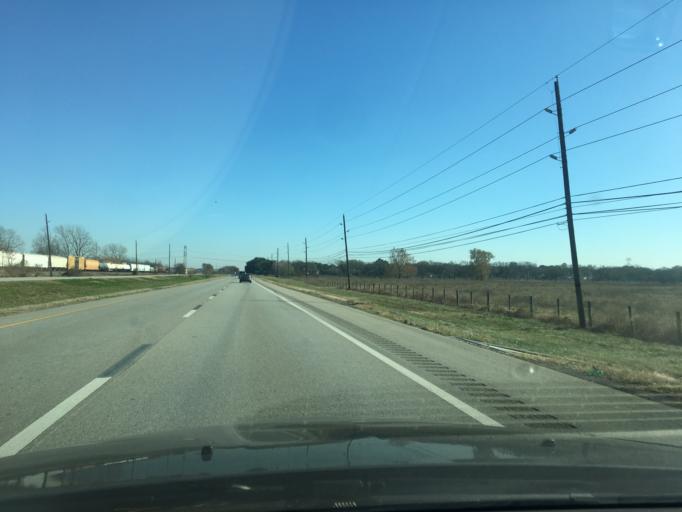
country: US
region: Texas
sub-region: Fort Bend County
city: New Territory
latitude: 29.5998
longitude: -95.7026
